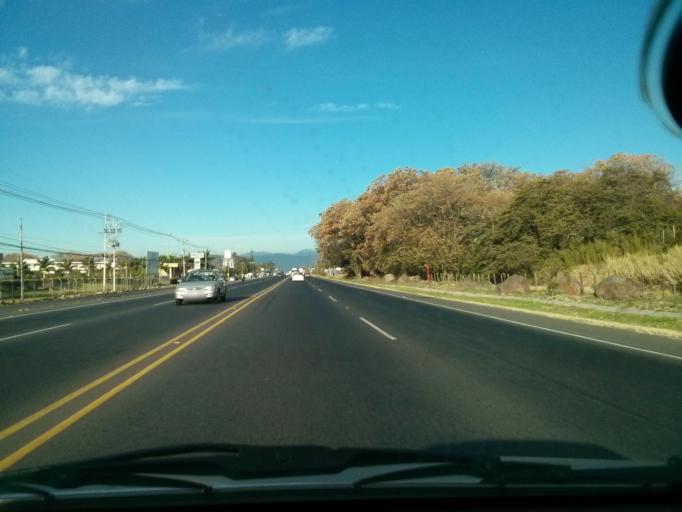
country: CR
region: Alajuela
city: Carrillos
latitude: 9.9953
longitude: -84.2594
